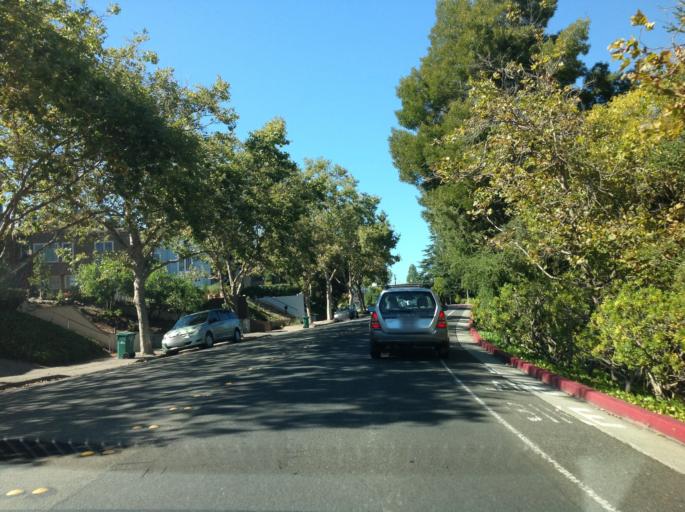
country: US
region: California
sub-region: Alameda County
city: Piedmont
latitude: 37.8269
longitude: -122.2436
